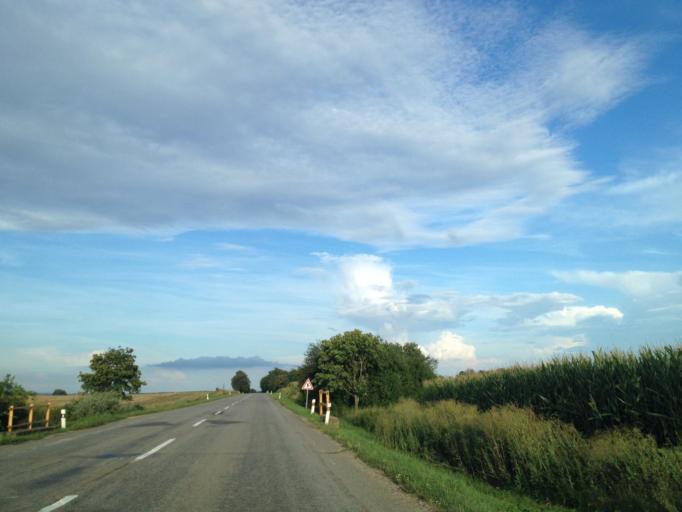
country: SK
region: Nitriansky
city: Svodin
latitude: 47.9017
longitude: 18.3541
